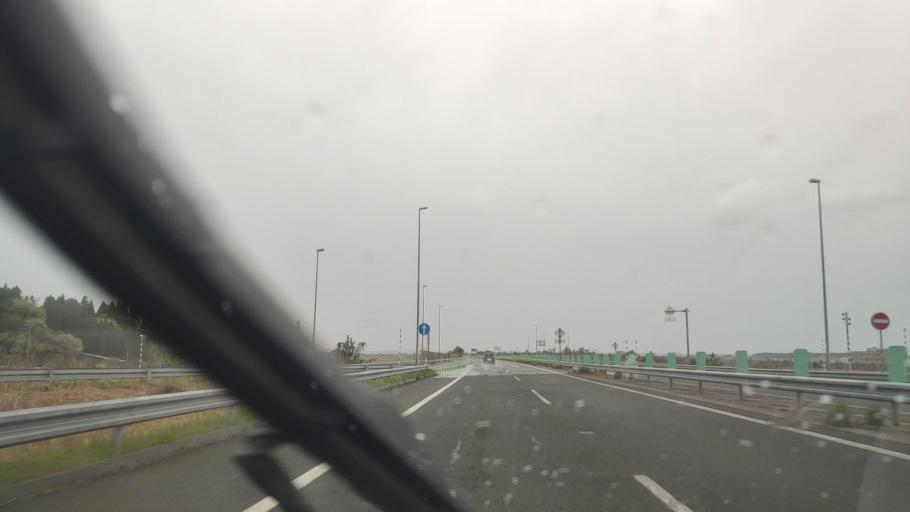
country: JP
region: Akita
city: Noshiromachi
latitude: 40.1842
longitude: 140.0828
